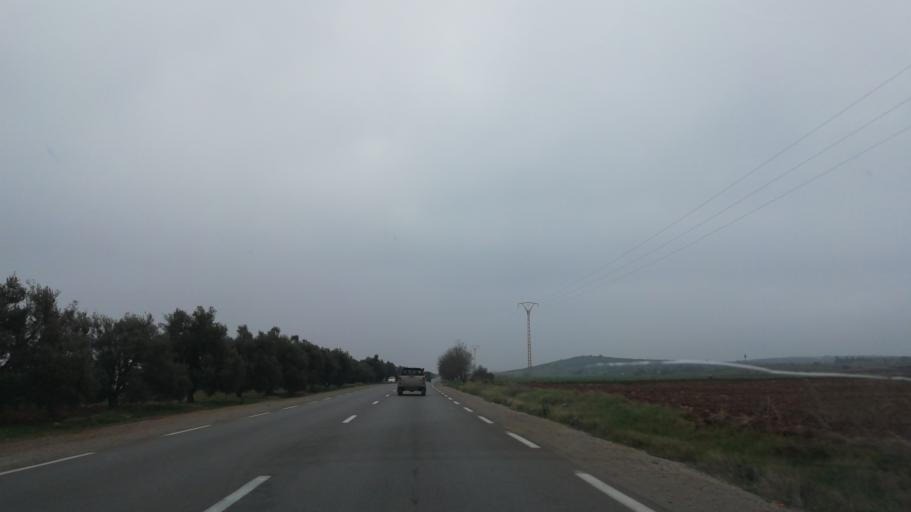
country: DZ
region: Mascara
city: Mascara
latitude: 35.3128
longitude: 0.3889
